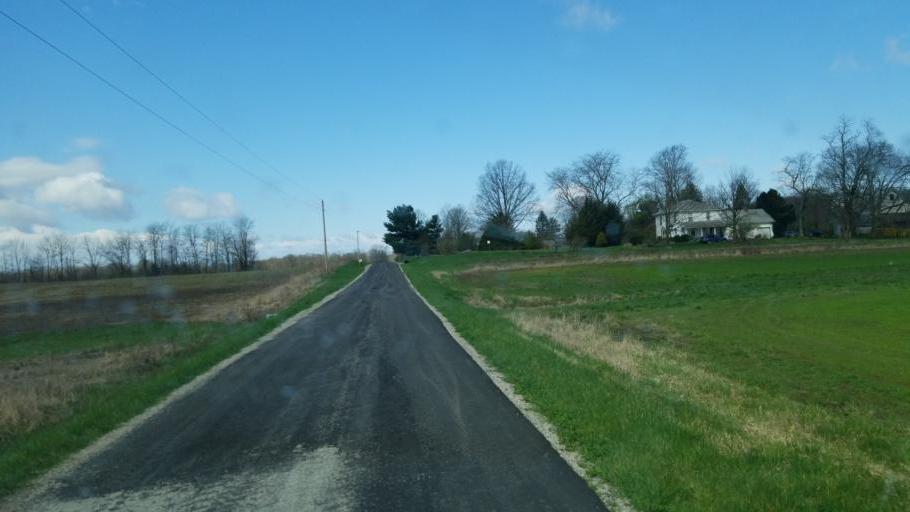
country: US
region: Ohio
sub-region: Delaware County
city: Ashley
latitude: 40.3905
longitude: -83.0288
